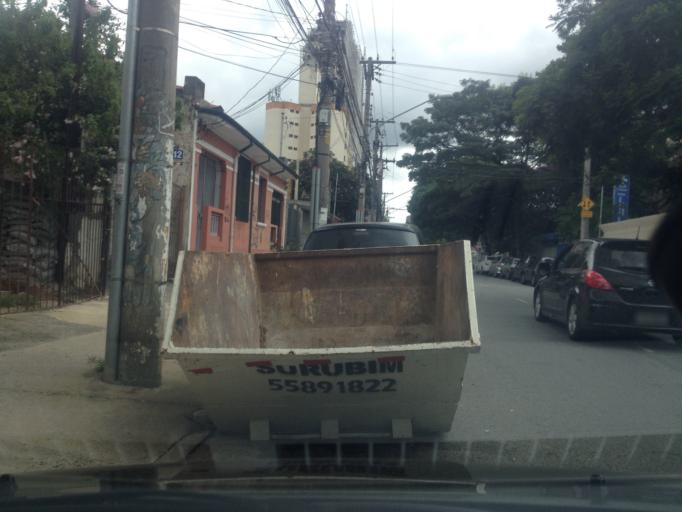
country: BR
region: Sao Paulo
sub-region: Sao Paulo
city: Sao Paulo
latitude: -23.5651
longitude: -46.6981
